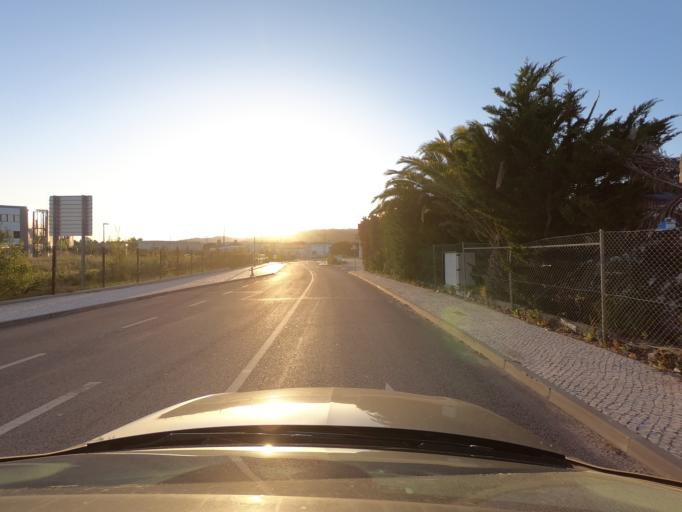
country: PT
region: Lisbon
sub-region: Cascais
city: Alcabideche
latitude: 38.7580
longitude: -9.3758
